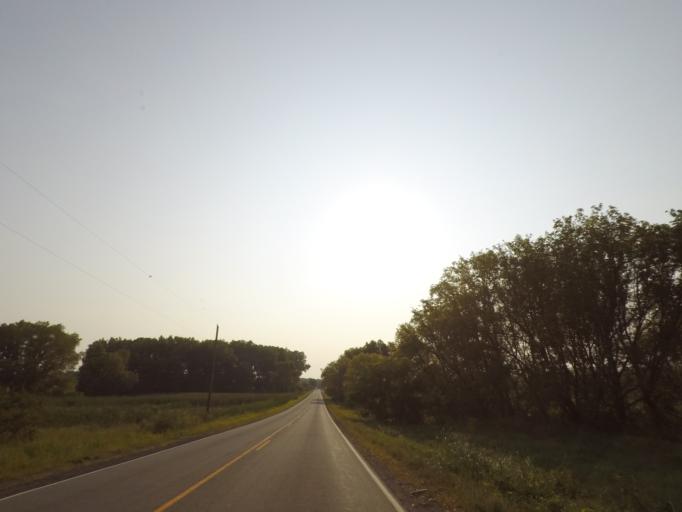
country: US
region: Wisconsin
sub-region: Dane County
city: McFarland
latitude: 43.0522
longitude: -89.2641
